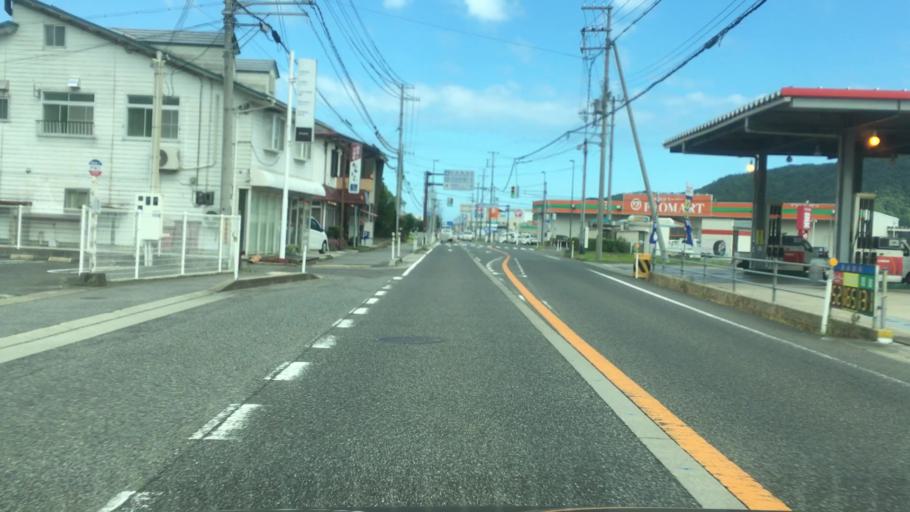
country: JP
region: Tottori
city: Tottori
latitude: 35.6139
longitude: 134.4669
